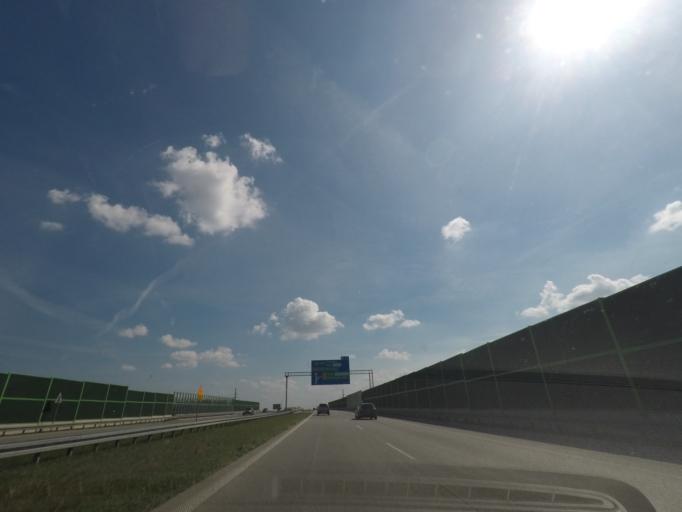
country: PL
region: Lodz Voivodeship
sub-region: Powiat lodzki wschodni
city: Andrespol
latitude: 51.7558
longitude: 19.5951
